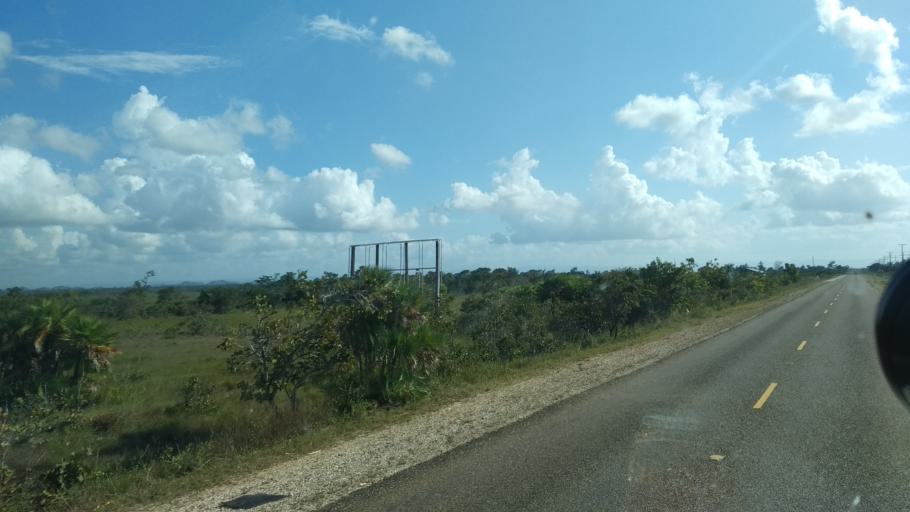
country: BZ
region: Cayo
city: Belmopan
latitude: 17.3971
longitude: -88.5085
